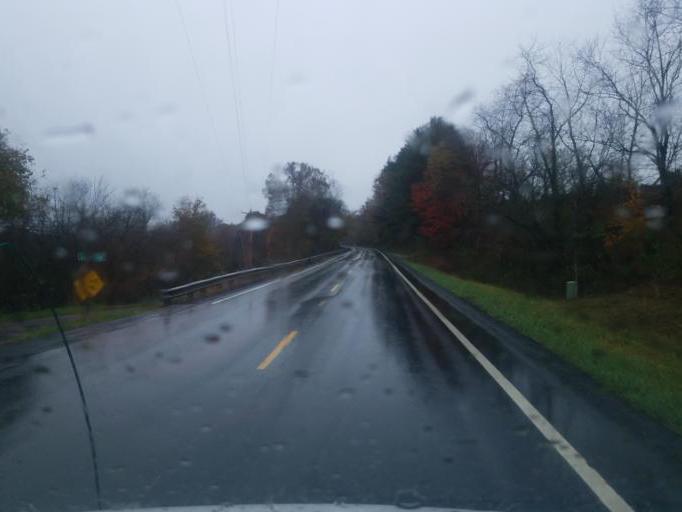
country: US
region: Ohio
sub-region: Washington County
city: Beverly
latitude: 39.4595
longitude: -81.6387
